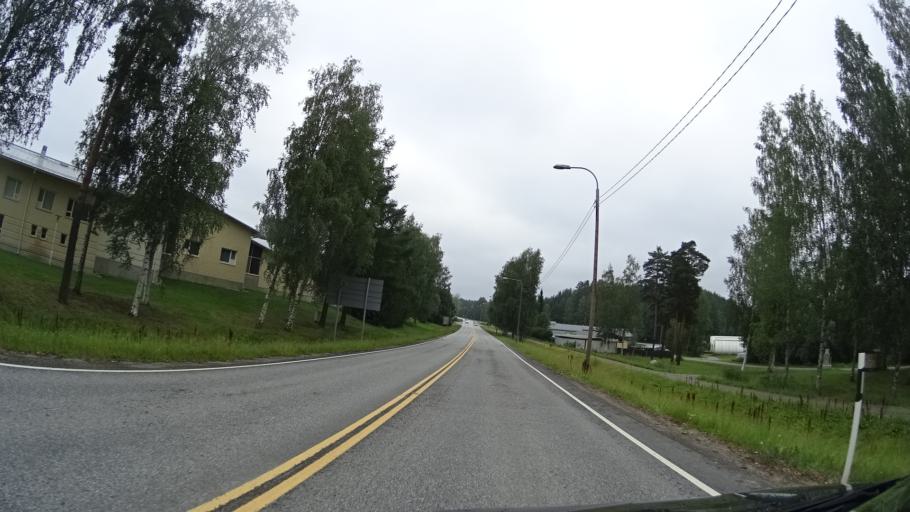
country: FI
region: Southern Savonia
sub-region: Savonlinna
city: Punkaharju
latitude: 61.7573
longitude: 29.3918
